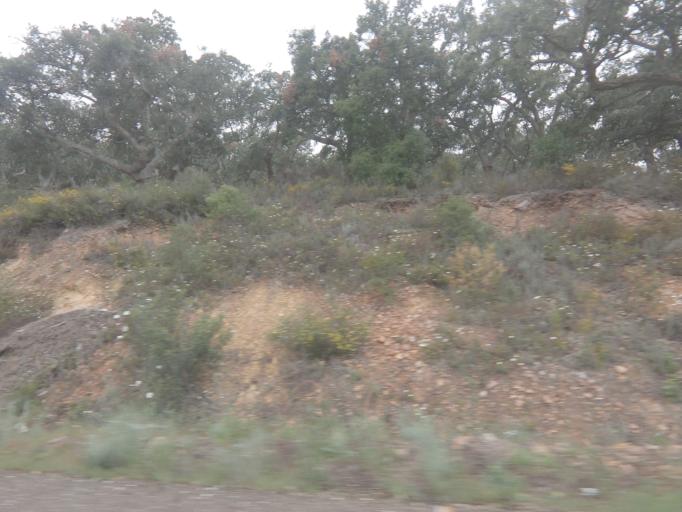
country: ES
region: Extremadura
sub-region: Provincia de Badajoz
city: Puebla de Obando
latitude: 39.1869
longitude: -6.6002
